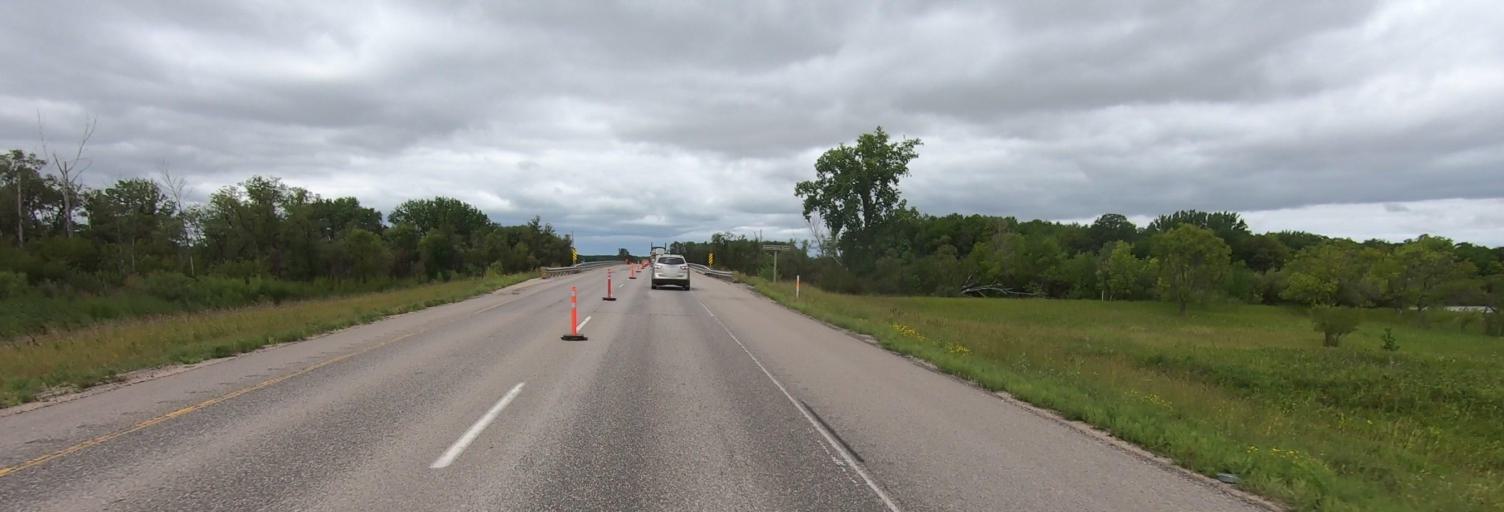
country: CA
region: Manitoba
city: Portage la Prairie
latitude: 49.9708
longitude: -98.0961
